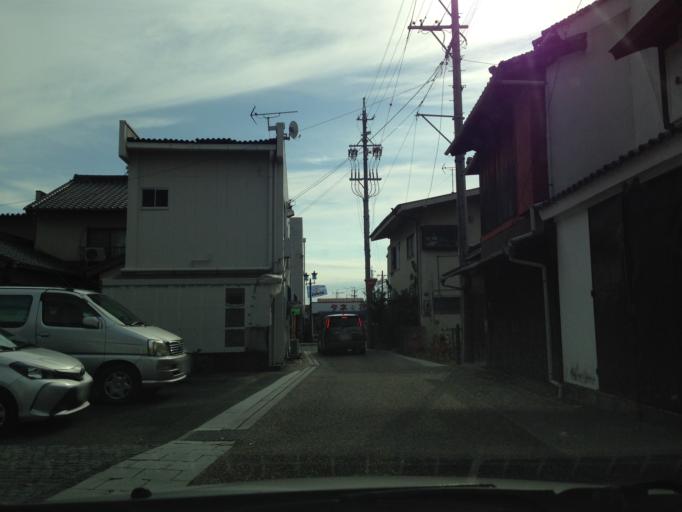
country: JP
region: Shizuoka
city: Iwata
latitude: 34.7270
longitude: 137.8556
